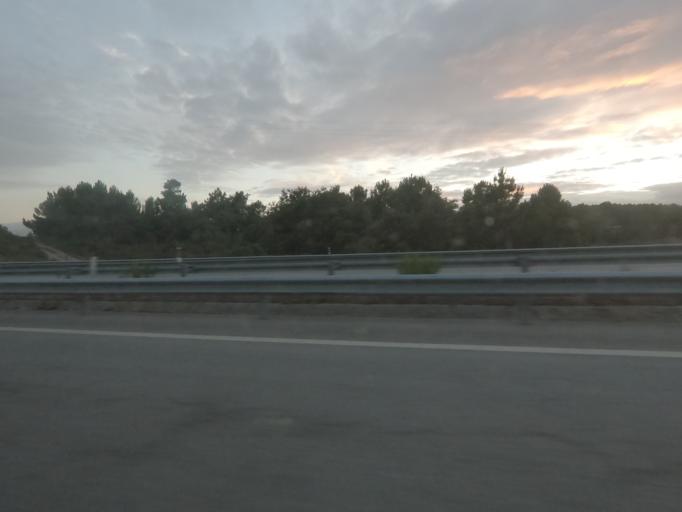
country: PT
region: Vila Real
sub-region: Vila Real
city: Vila Real
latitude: 41.2883
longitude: -7.6917
